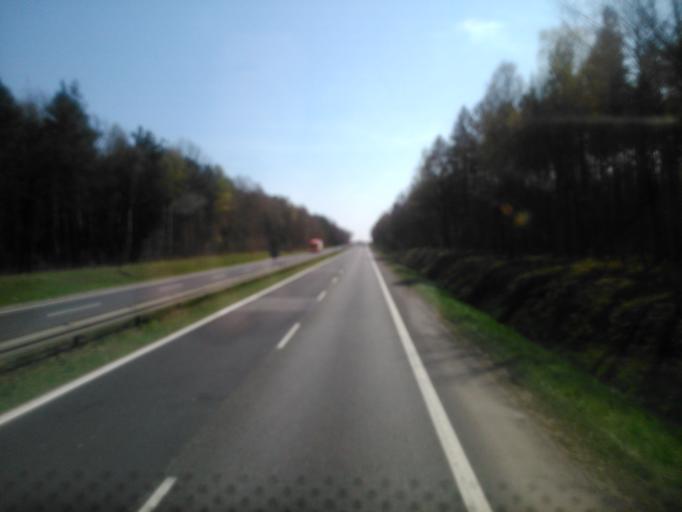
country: PL
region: Silesian Voivodeship
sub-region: Powiat czestochowski
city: Kamienica Polska
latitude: 50.6484
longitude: 19.1336
